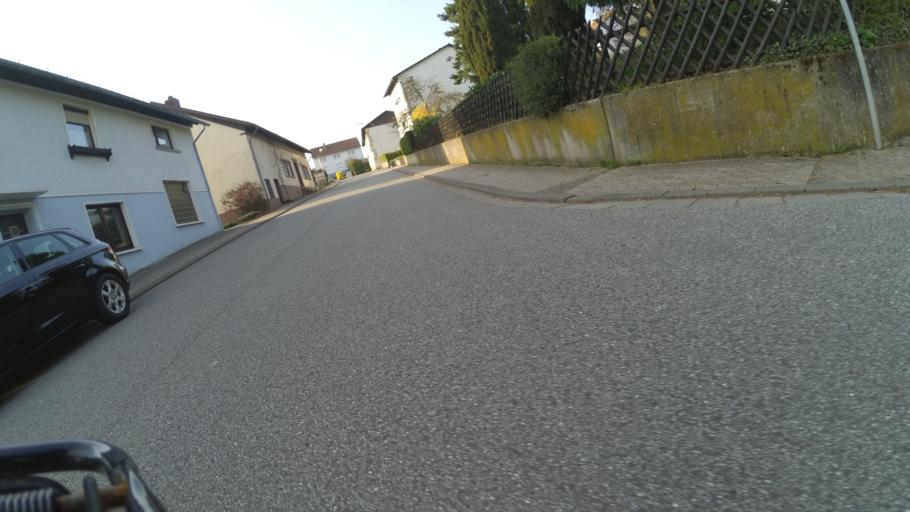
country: DE
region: Saarland
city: Heusweiler
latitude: 49.3479
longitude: 6.9834
